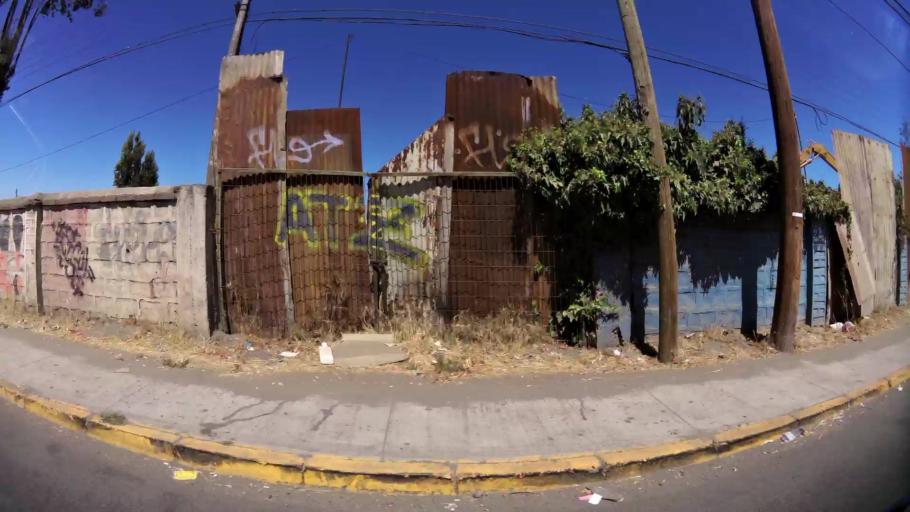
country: CL
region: O'Higgins
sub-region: Provincia de Cachapoal
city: Rancagua
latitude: -34.1658
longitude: -70.7718
